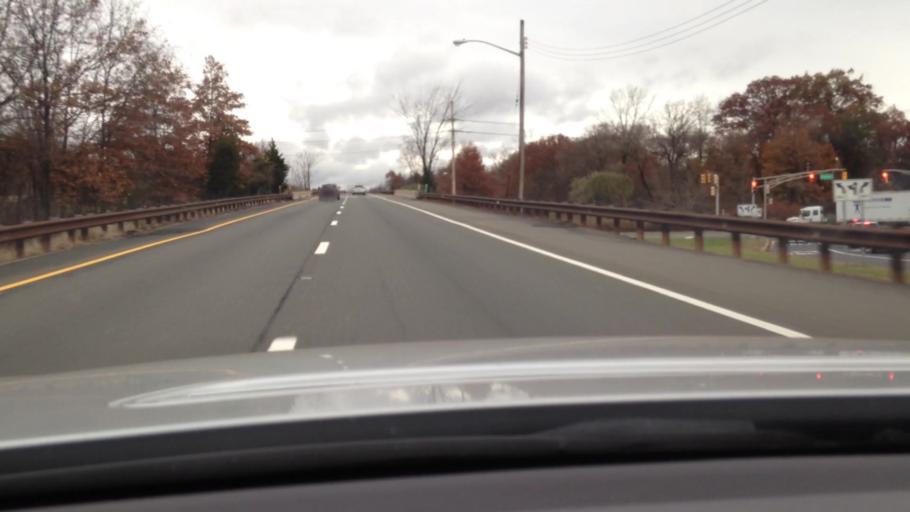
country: US
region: New Jersey
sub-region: Bergen County
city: Park Ridge
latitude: 41.0544
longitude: -74.0651
